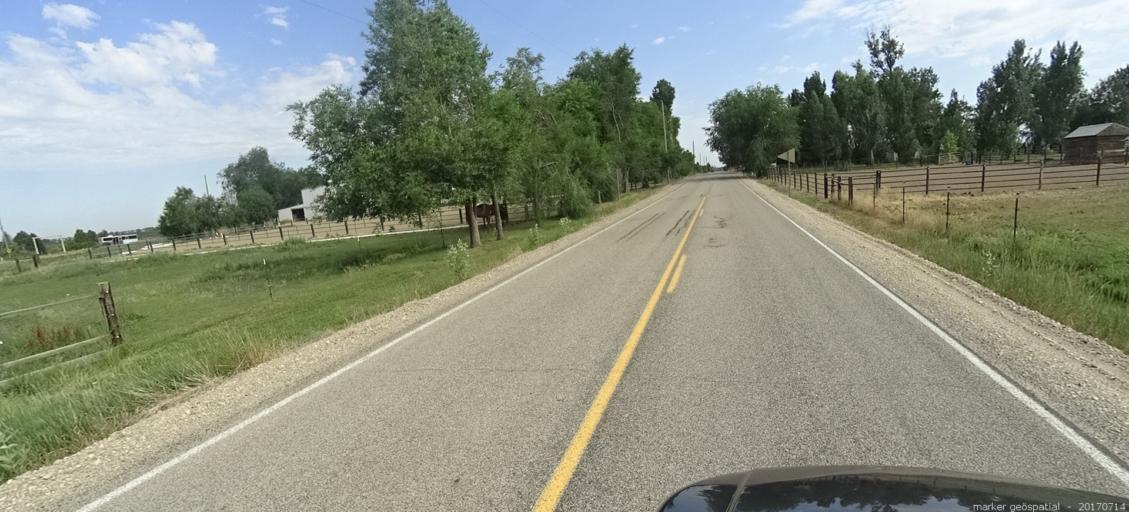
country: US
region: Idaho
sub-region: Ada County
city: Kuna
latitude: 43.4902
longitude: -116.3544
